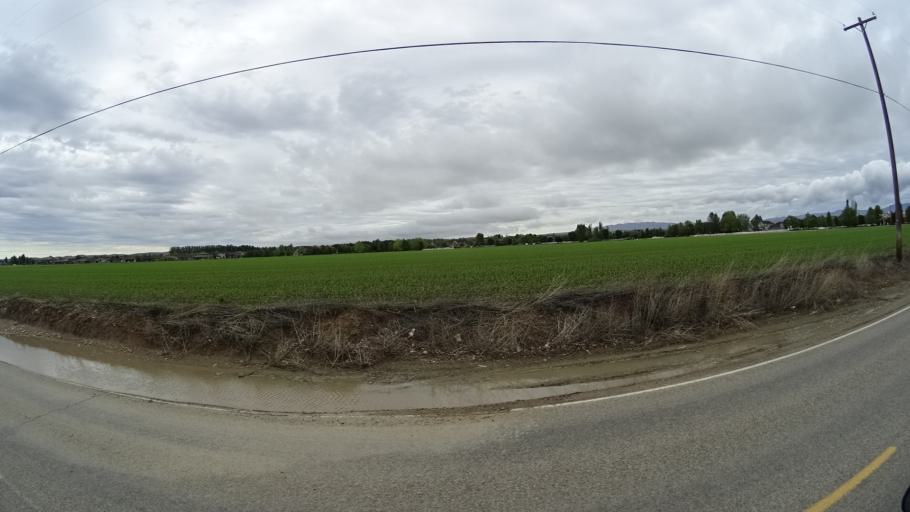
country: US
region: Idaho
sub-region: Ada County
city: Eagle
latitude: 43.7061
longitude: -116.4067
